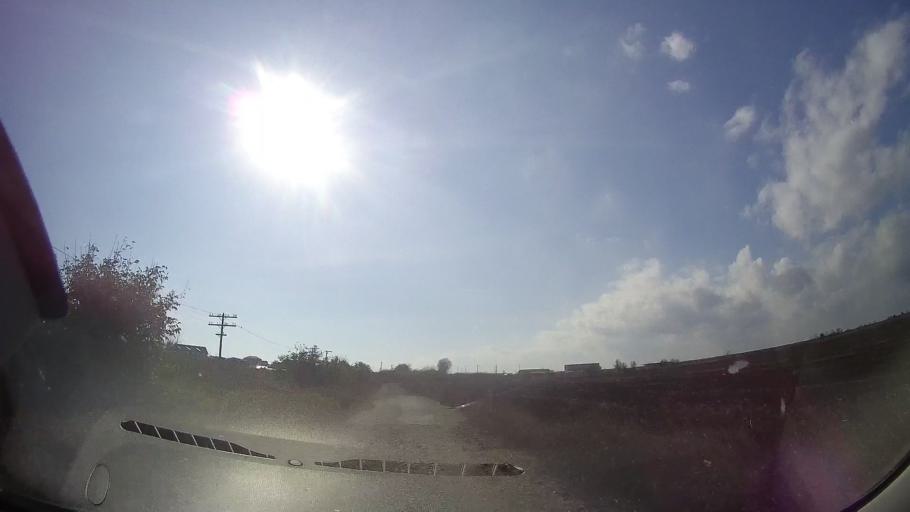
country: RO
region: Constanta
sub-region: Comuna Costinesti
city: Costinesti
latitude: 43.9649
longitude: 28.6394
